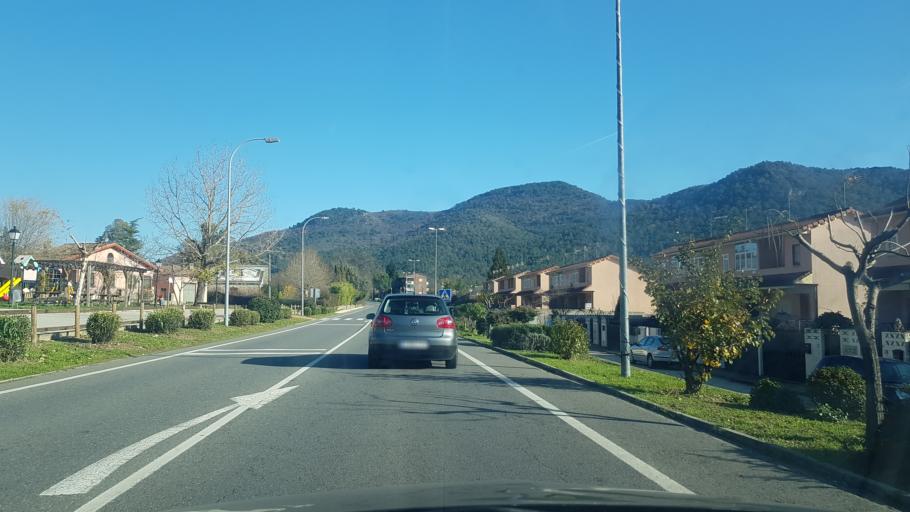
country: ES
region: Castille and Leon
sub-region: Provincia de Avila
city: Casillas
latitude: 40.3020
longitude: -4.5479
